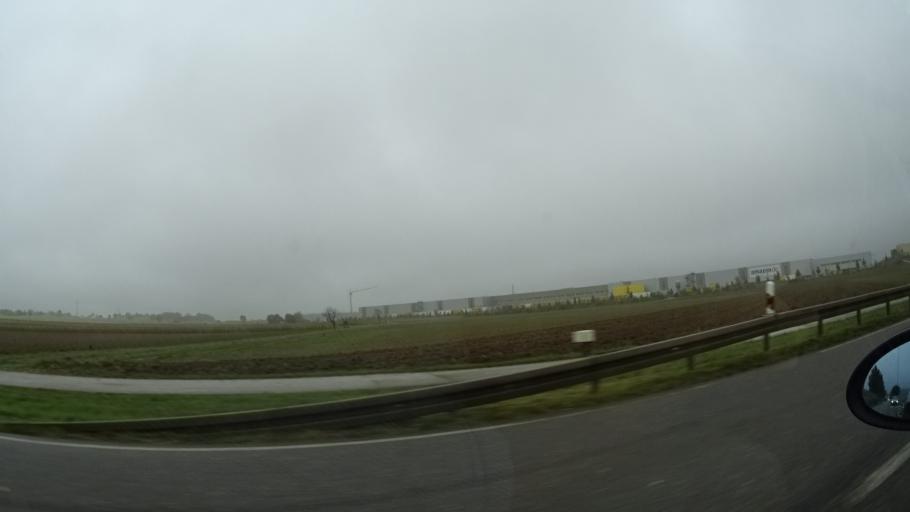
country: DE
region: Baden-Wuerttemberg
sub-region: Karlsruhe Region
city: Kieselbronn
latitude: 48.9273
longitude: 8.7195
